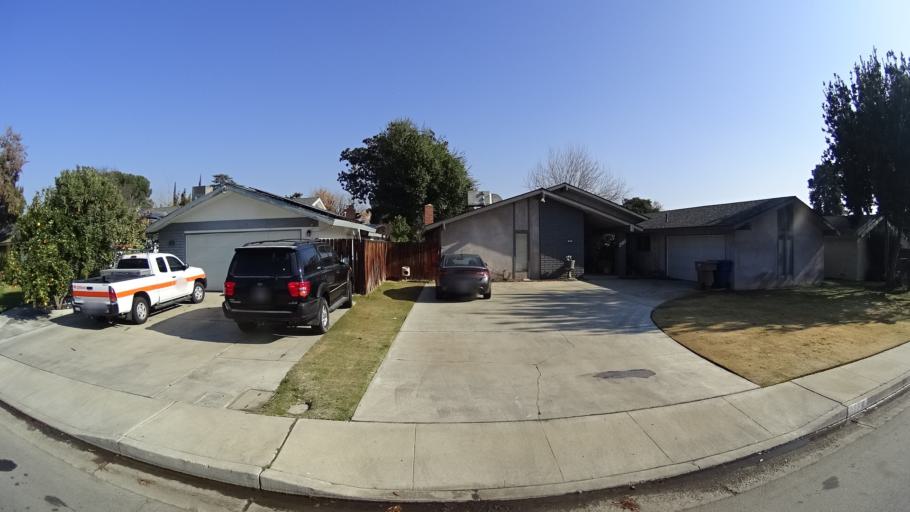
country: US
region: California
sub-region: Kern County
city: Greenacres
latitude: 35.3605
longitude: -119.0679
